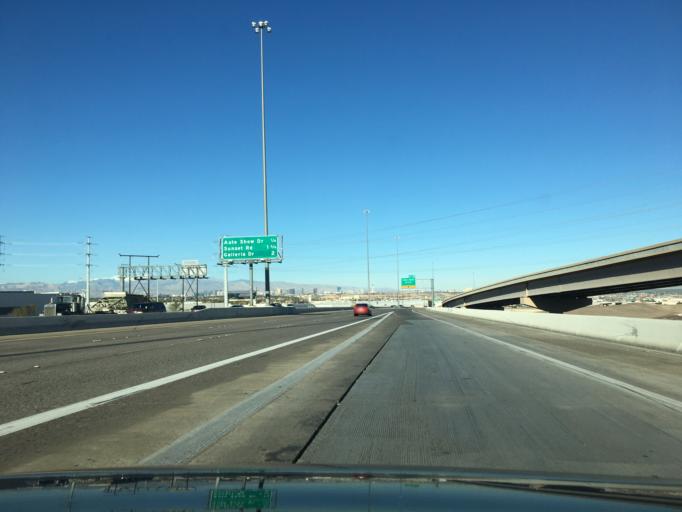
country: US
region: Nevada
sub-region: Clark County
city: Henderson
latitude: 36.0369
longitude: -115.0172
